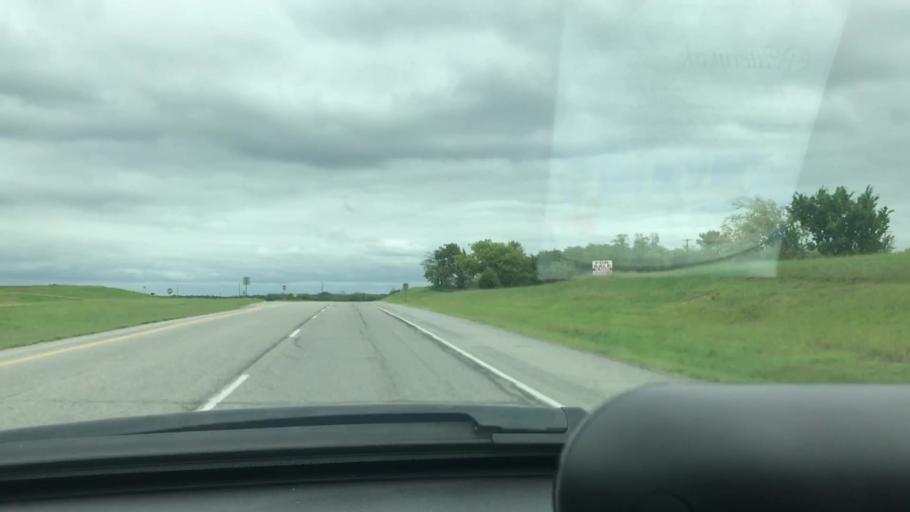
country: US
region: Oklahoma
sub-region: Wagoner County
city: Wagoner
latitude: 35.9907
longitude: -95.3724
